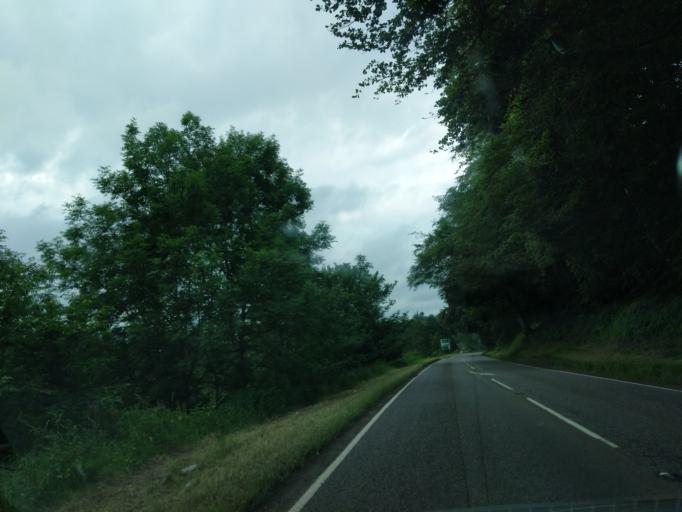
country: GB
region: Scotland
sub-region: Moray
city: Rothes
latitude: 57.4943
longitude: -3.1903
